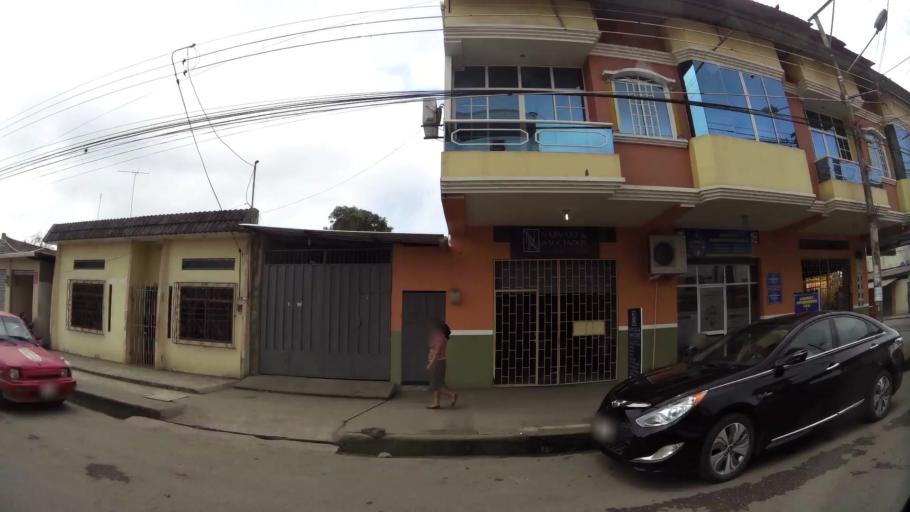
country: EC
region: El Oro
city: Pasaje
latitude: -3.2433
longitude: -79.8308
